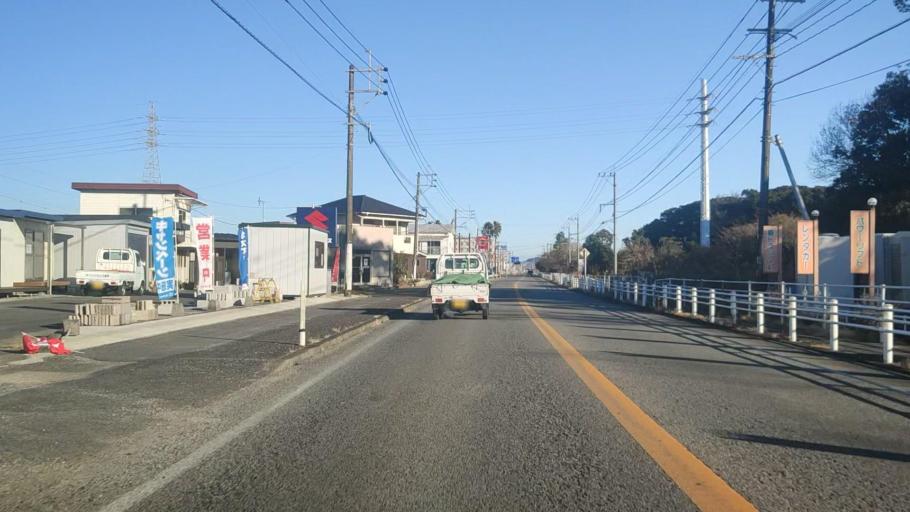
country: JP
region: Miyazaki
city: Nobeoka
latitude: 32.3908
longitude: 131.6277
